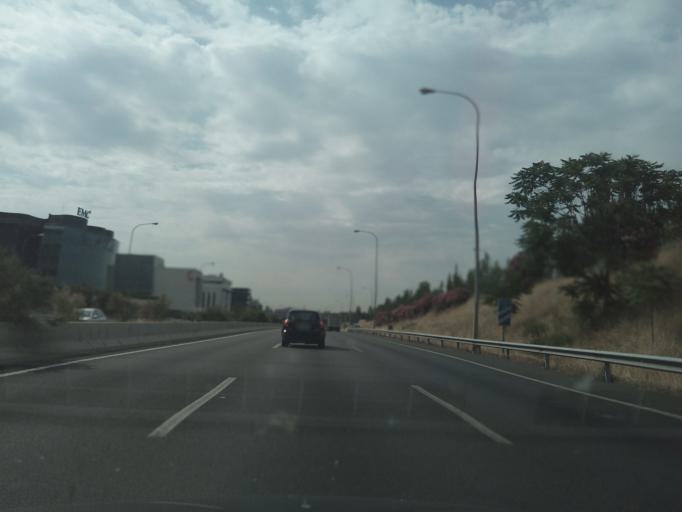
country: ES
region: Madrid
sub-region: Provincia de Madrid
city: Hortaleza
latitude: 40.4680
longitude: -3.6276
